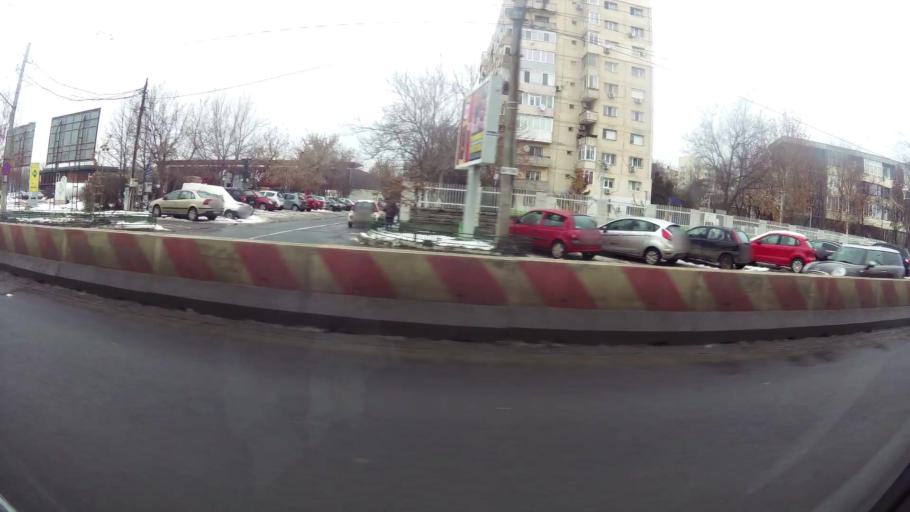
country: RO
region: Ilfov
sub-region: Comuna Chiajna
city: Rosu
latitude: 44.4179
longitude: 26.0365
